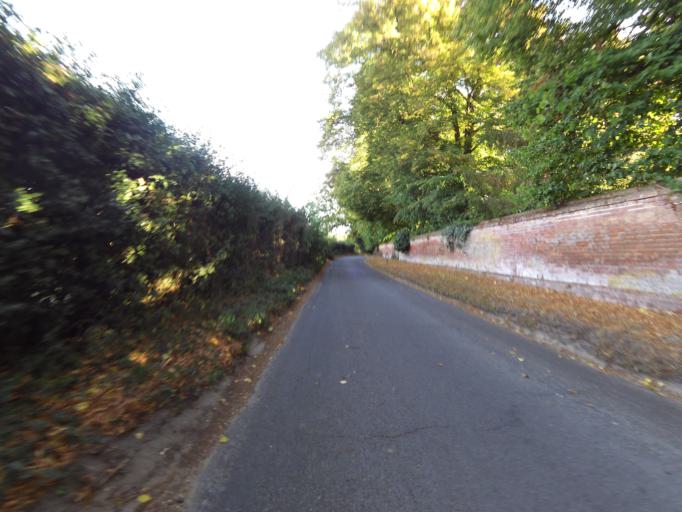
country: GB
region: England
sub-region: Suffolk
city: Kesgrave
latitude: 52.0126
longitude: 1.2287
